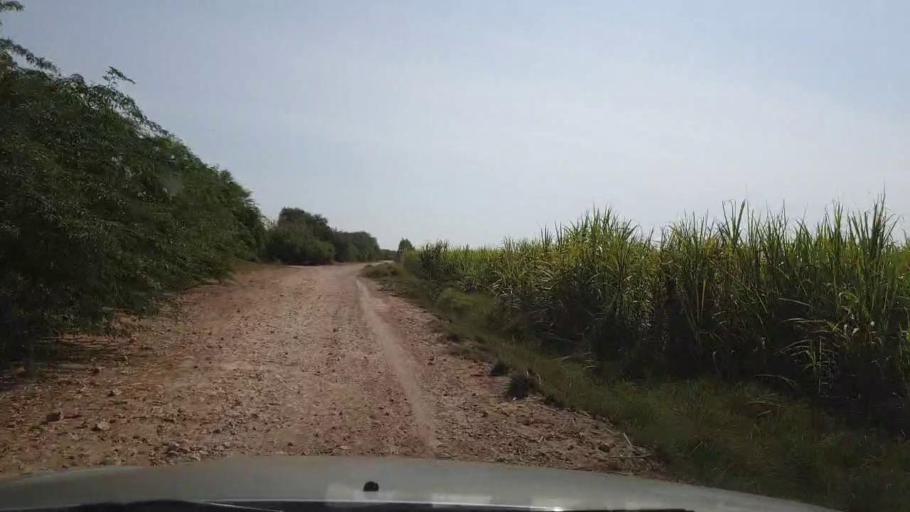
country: PK
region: Sindh
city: Bulri
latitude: 25.0104
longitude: 68.3201
